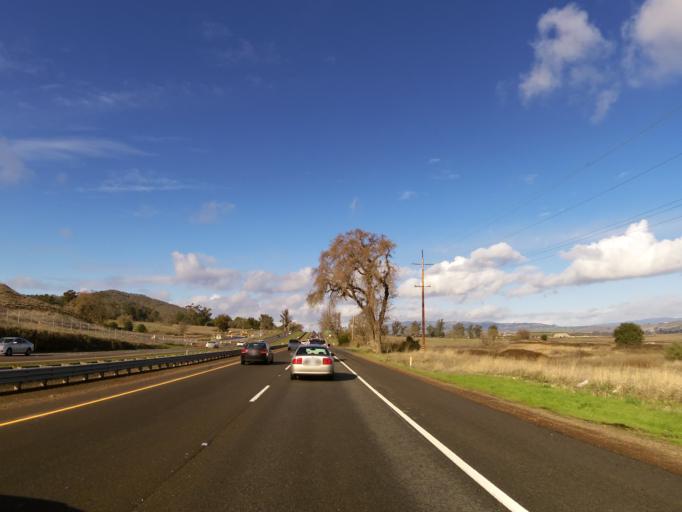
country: US
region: California
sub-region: Marin County
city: Novato
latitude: 38.1474
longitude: -122.5654
